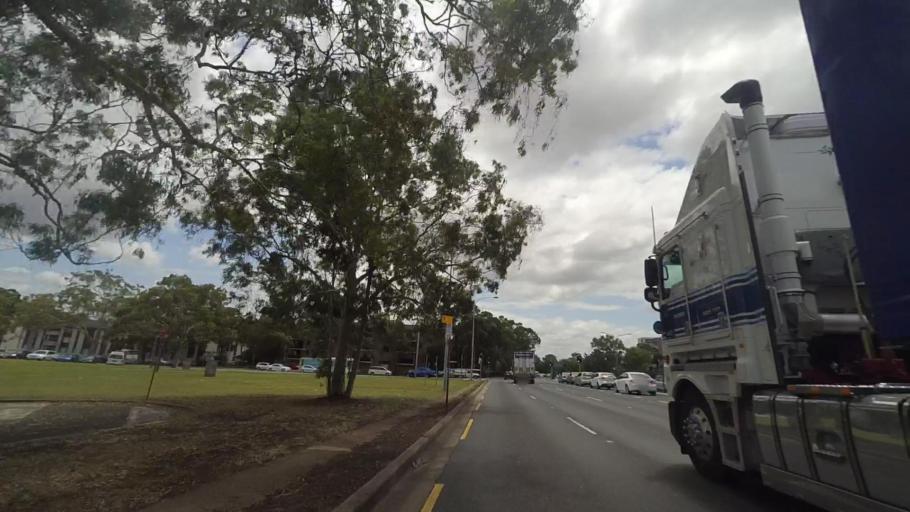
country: AU
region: New South Wales
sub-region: Fairfield
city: Cabramatta West
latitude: -33.9249
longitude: 150.9180
